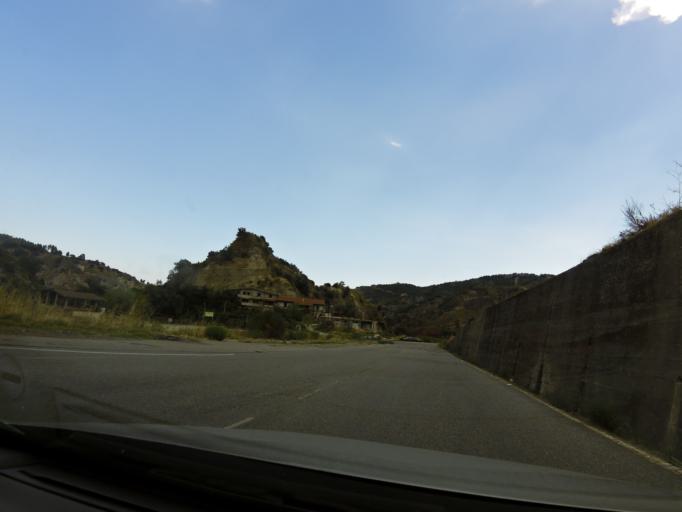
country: IT
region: Calabria
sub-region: Provincia di Reggio Calabria
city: Stilo
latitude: 38.4709
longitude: 16.4809
